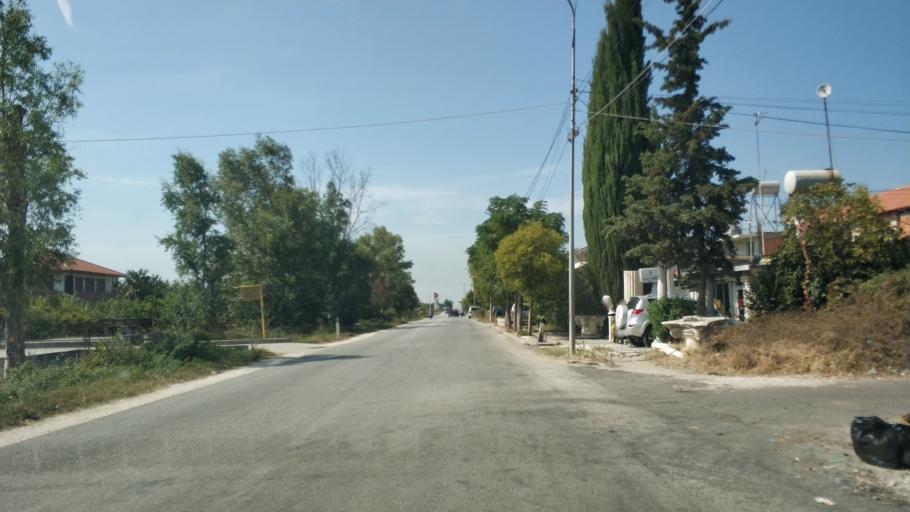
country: AL
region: Fier
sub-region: Rrethi i Fierit
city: Dermenas
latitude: 40.7368
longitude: 19.5205
